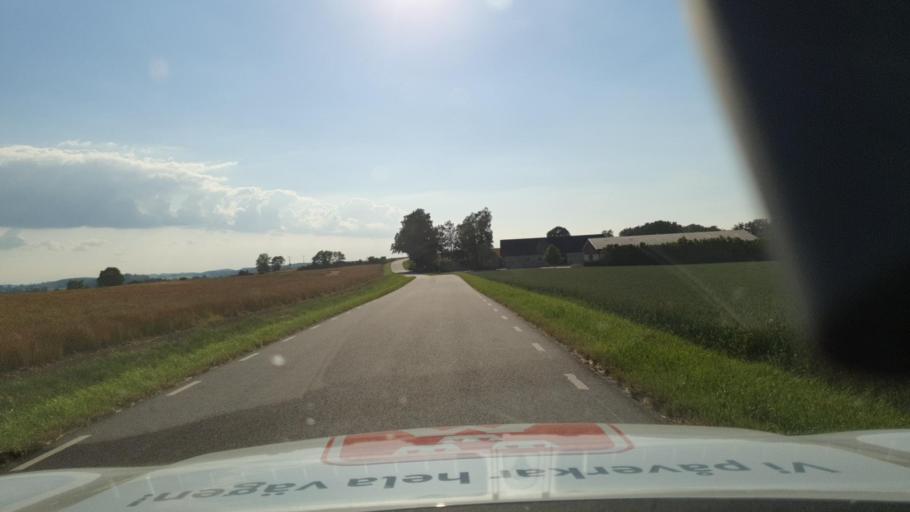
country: SE
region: Skane
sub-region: Skurups Kommun
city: Rydsgard
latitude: 55.5056
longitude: 13.5655
